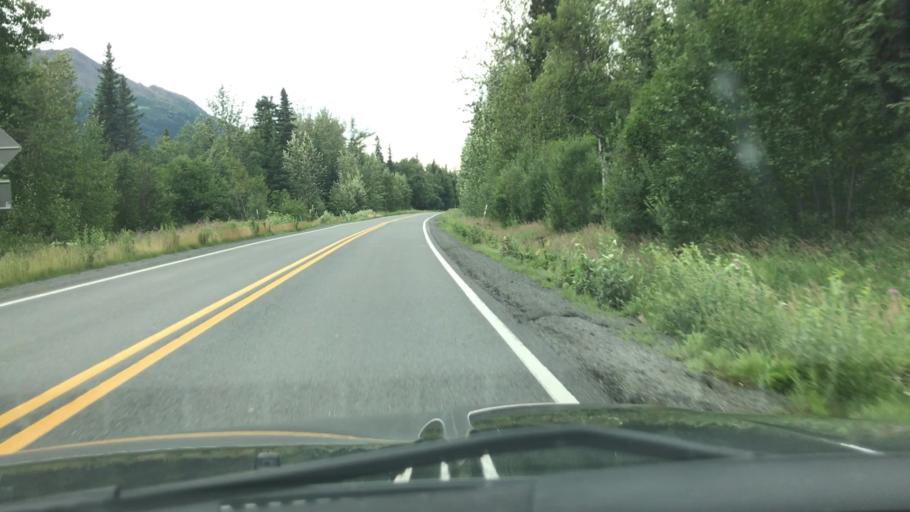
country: US
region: Alaska
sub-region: Kenai Peninsula Borough
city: Seward
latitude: 60.4876
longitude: -149.9827
